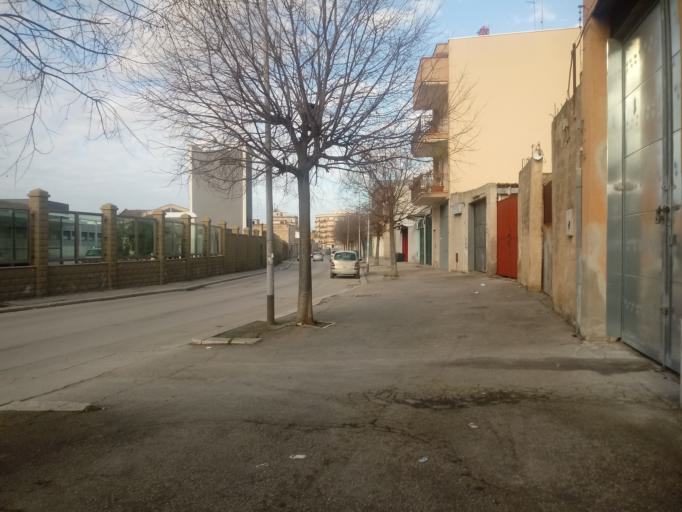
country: IT
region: Apulia
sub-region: Provincia di Barletta - Andria - Trani
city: Andria
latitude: 41.2181
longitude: 16.2965
